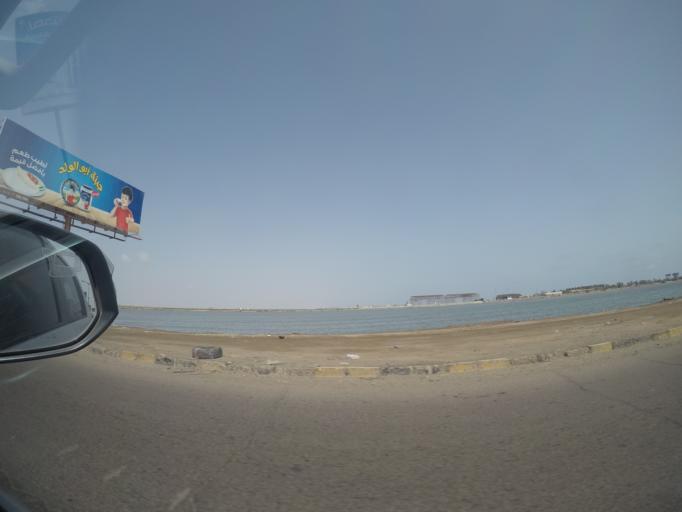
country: YE
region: Aden
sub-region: Khur Maksar
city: Khawr Maksar
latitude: 12.8221
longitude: 45.0356
